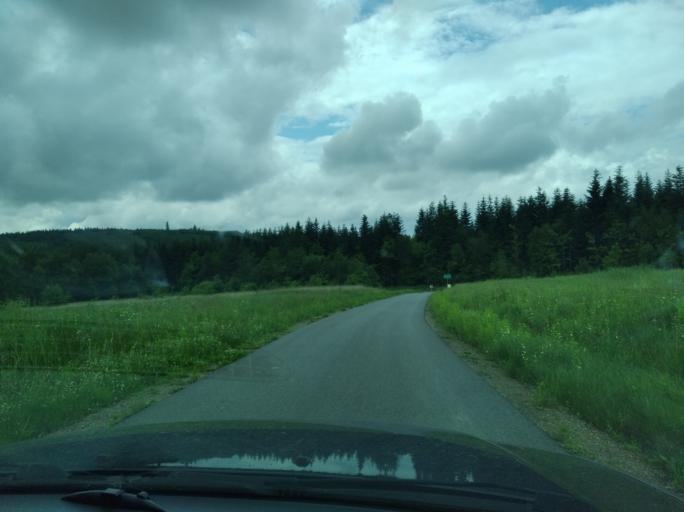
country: PL
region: Subcarpathian Voivodeship
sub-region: Powiat przemyski
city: Przedmiescie Dubieckie
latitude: 49.8771
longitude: 22.4037
